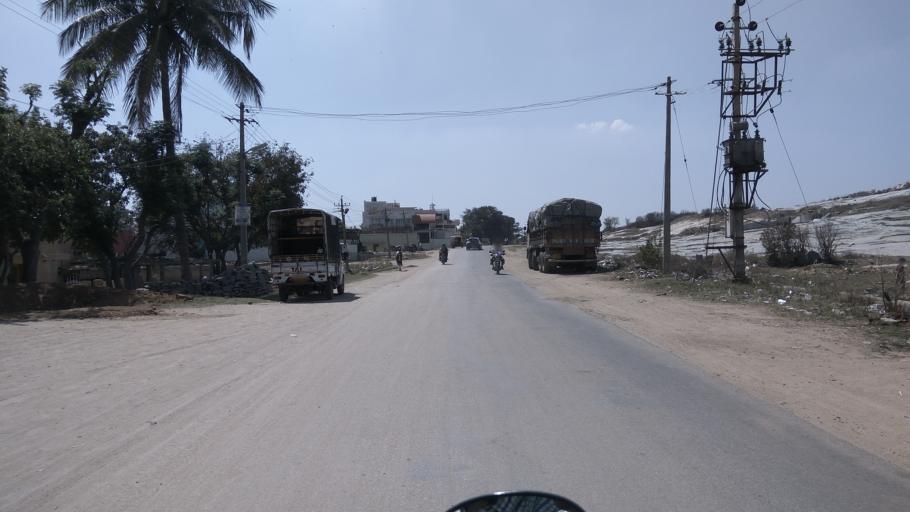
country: IN
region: Karnataka
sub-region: Kolar
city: Mulbagal
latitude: 13.1619
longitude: 78.3826
